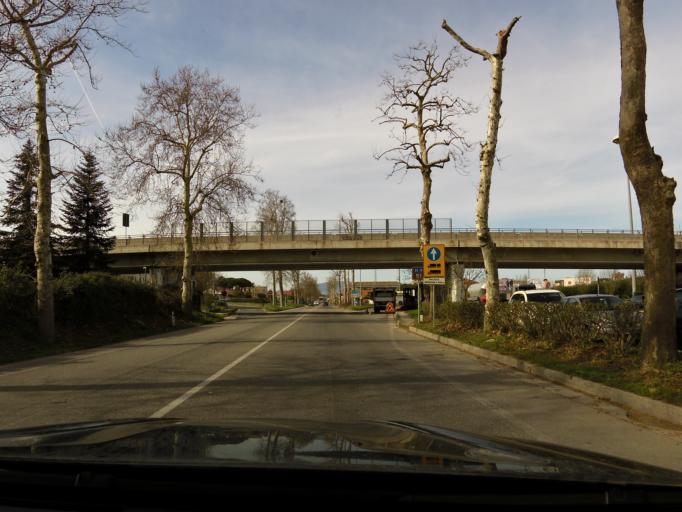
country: IT
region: The Marches
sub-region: Provincia di Macerata
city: Porto Recanati
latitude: 43.4306
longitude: 13.6609
